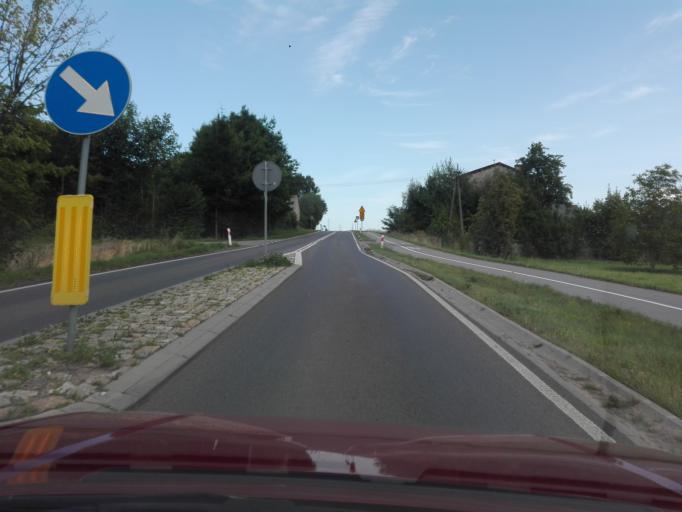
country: PL
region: West Pomeranian Voivodeship
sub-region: Powiat koszalinski
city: Sianow
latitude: 54.2961
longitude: 16.3055
